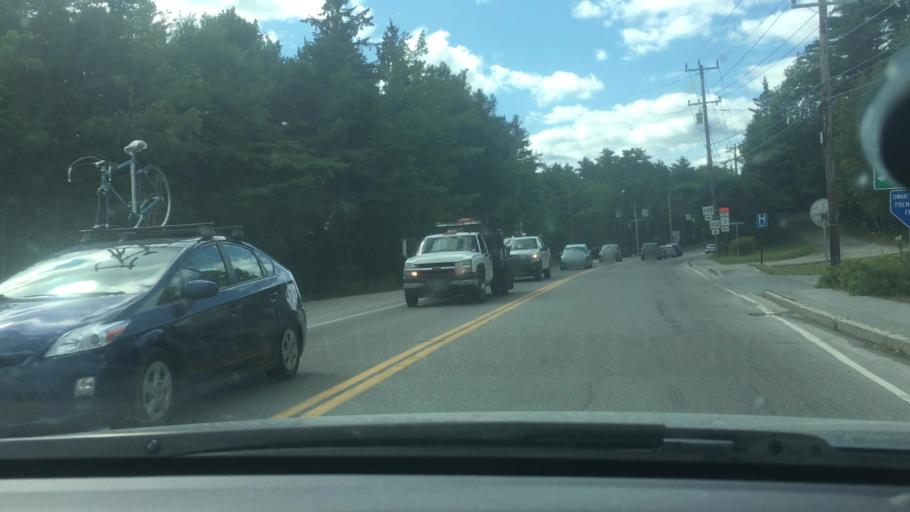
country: US
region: Maine
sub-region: Hancock County
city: Trenton
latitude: 44.3700
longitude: -68.3307
